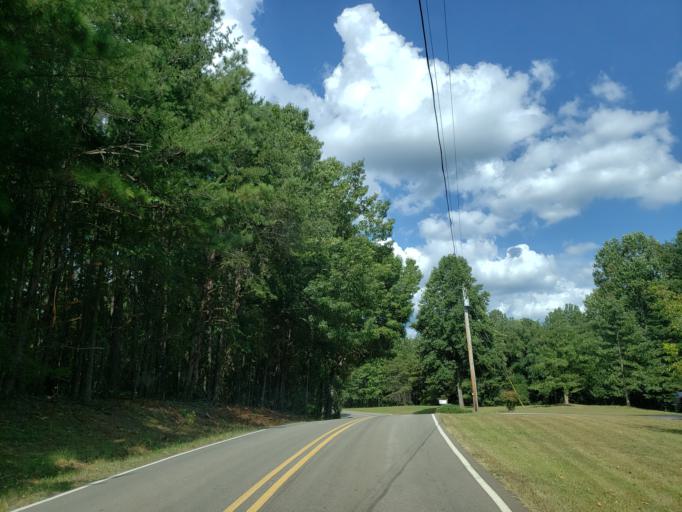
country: US
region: Georgia
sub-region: Pickens County
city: Jasper
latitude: 34.4211
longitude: -84.4446
